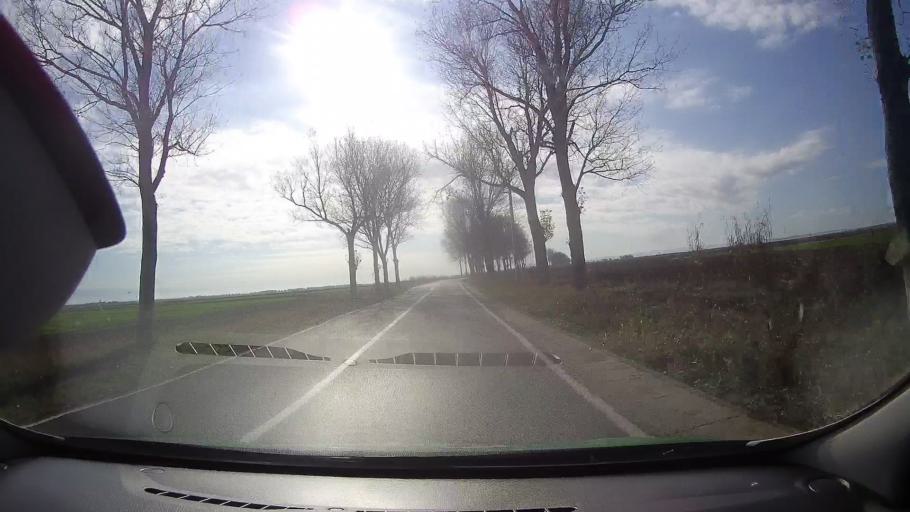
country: RO
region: Tulcea
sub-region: Comuna Valea Nucarilor
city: Agighiol
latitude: 44.9975
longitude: 28.8865
